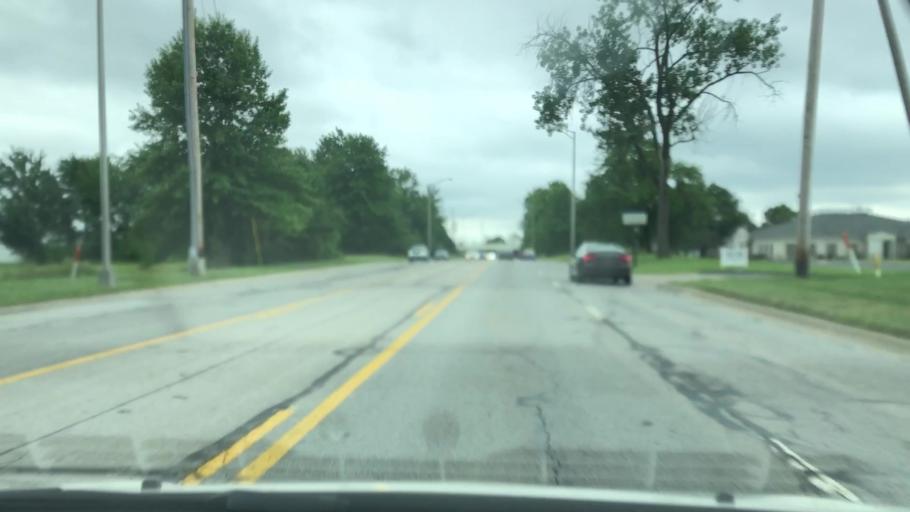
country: US
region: Ohio
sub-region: Franklin County
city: Worthington
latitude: 40.1150
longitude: -82.9959
